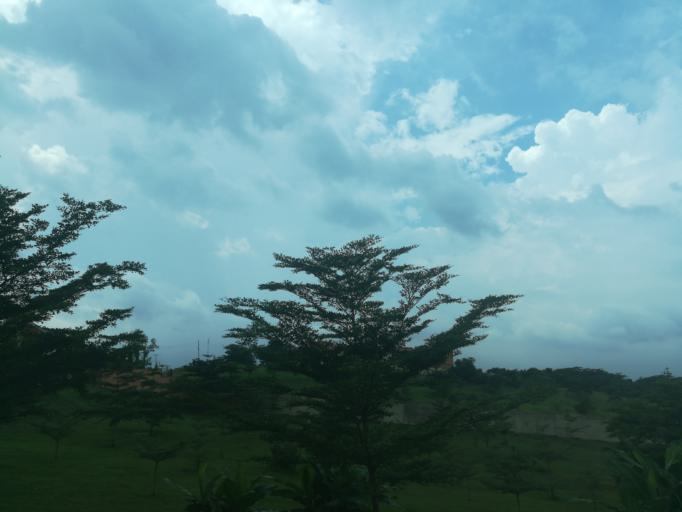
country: NG
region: Lagos
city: Ikorodu
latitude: 6.6675
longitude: 3.6412
